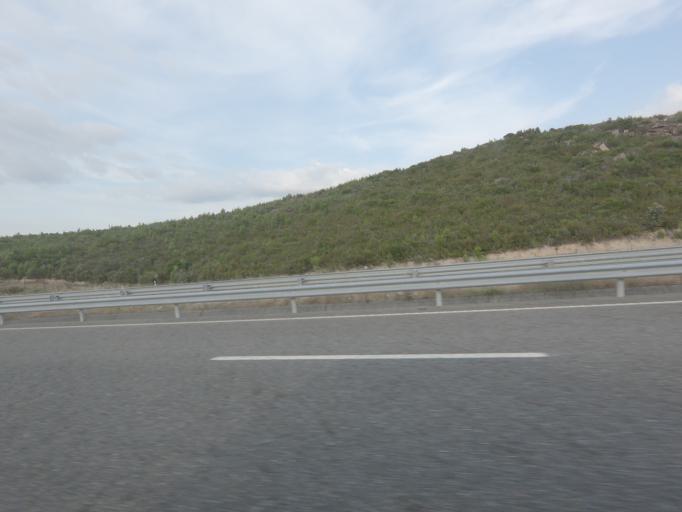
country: PT
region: Vila Real
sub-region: Boticas
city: Boticas
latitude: 41.6341
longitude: -7.5953
